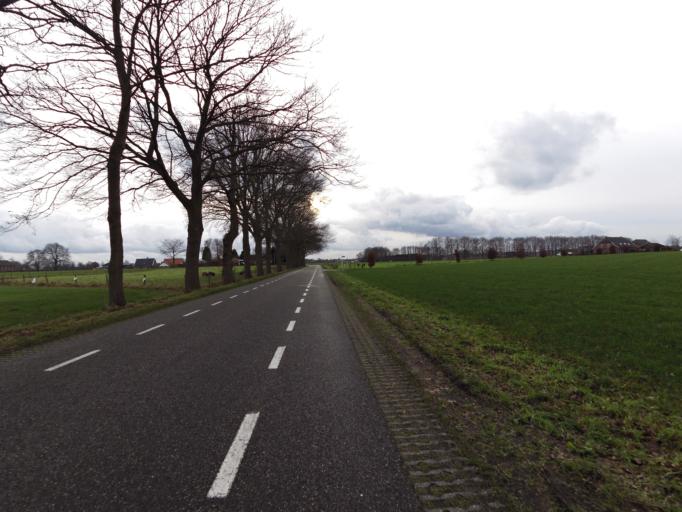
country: NL
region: Gelderland
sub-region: Oude IJsselstreek
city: Wisch
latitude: 51.9204
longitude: 6.4029
